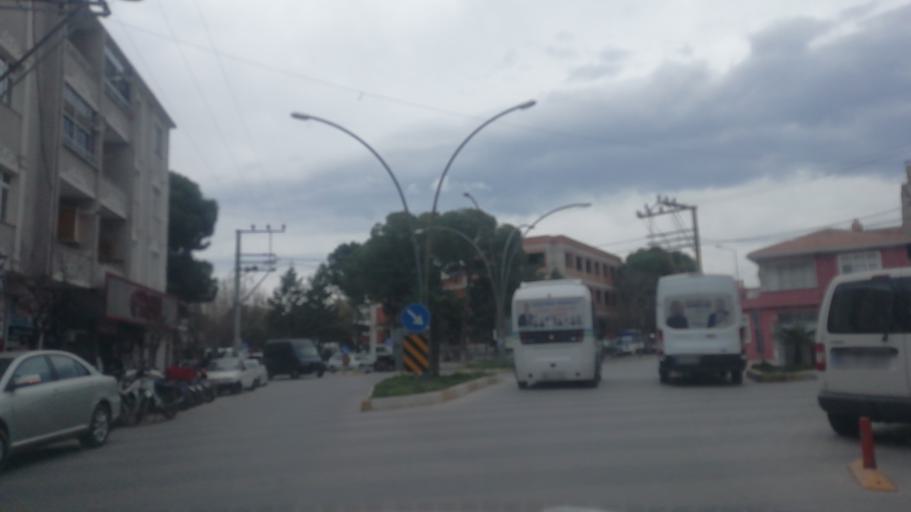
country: TR
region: Balikesir
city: Gonen
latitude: 40.1034
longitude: 27.6524
